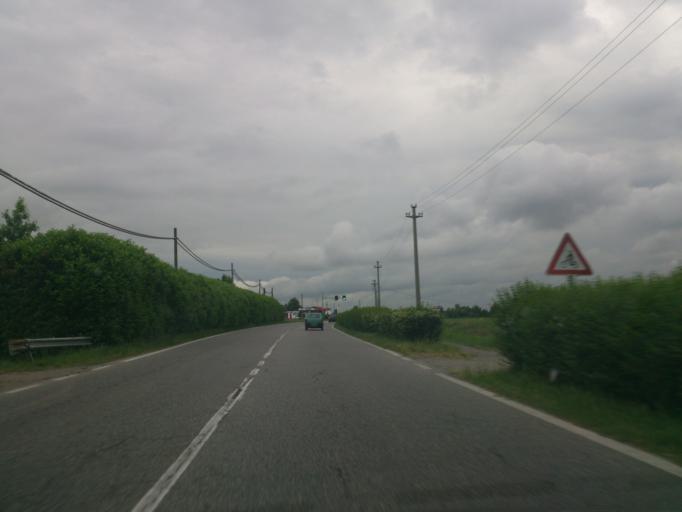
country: IT
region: Lombardy
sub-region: Citta metropolitana di Milano
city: Triginto
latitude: 45.4068
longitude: 9.3185
